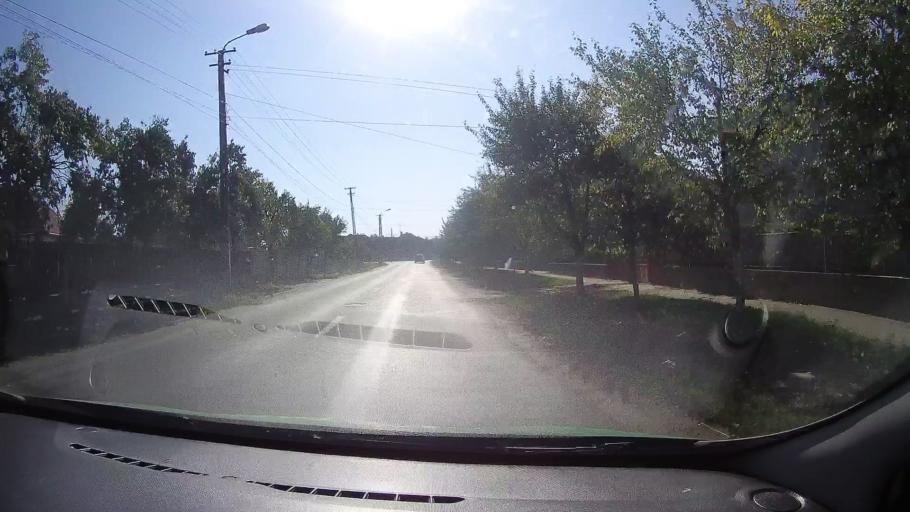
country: RO
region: Satu Mare
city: Carei
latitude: 47.6941
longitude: 22.4728
